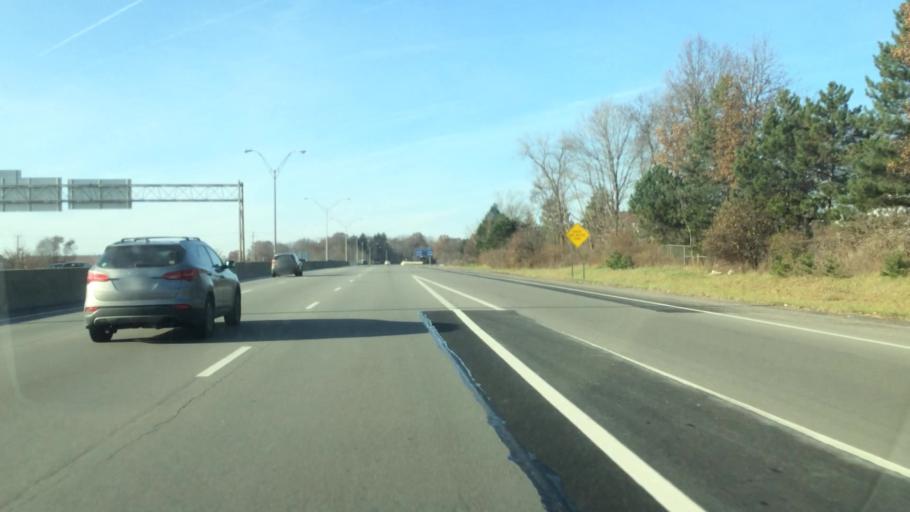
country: US
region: Ohio
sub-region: Summit County
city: Silver Lake
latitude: 41.1651
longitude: -81.4741
